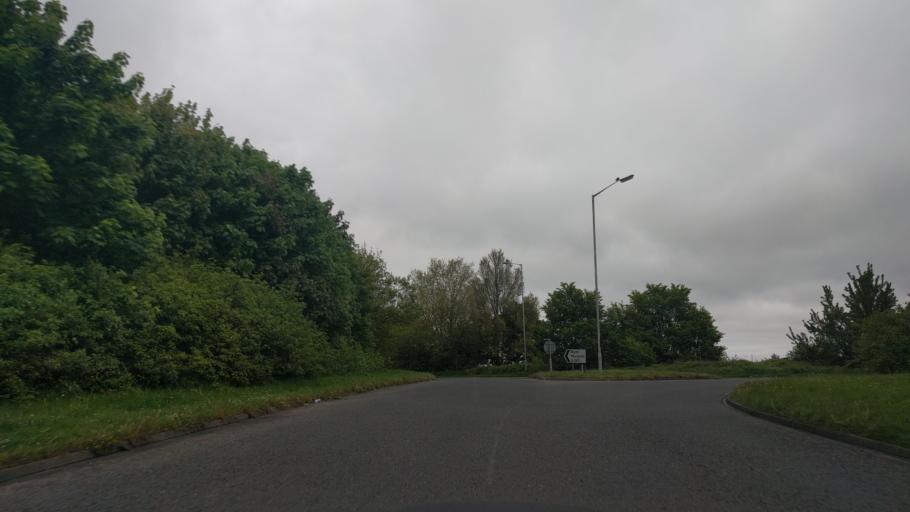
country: GB
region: England
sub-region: Northumberland
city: Cramlington
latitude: 55.0962
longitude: -1.5956
